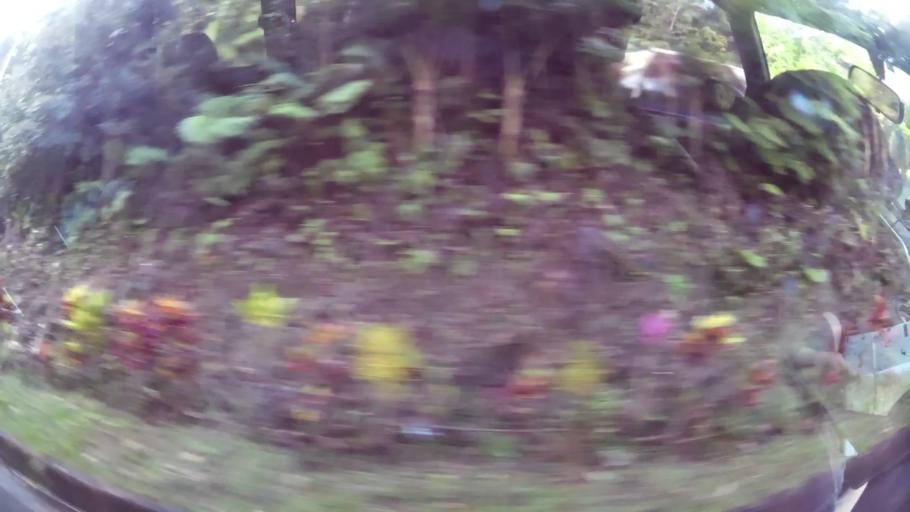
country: DM
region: Saint Paul
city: Pont Casse
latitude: 15.3712
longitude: -61.3500
